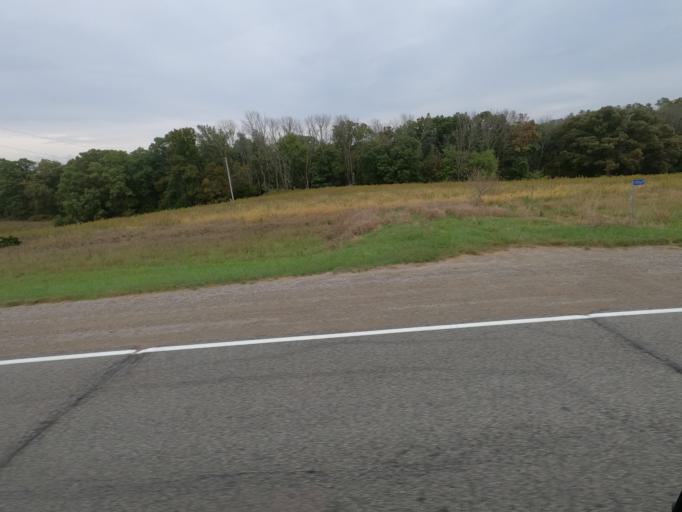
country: US
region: Iowa
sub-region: Van Buren County
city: Keosauqua
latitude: 40.8361
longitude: -91.9994
